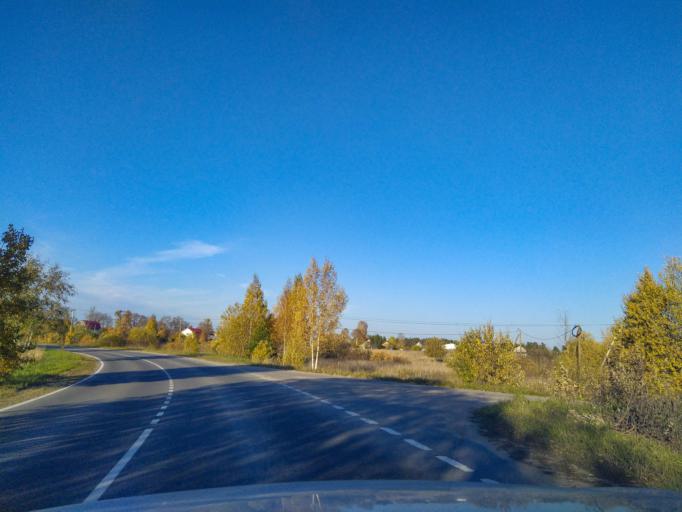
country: RU
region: Leningrad
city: Siverskiy
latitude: 59.3209
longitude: 30.0421
